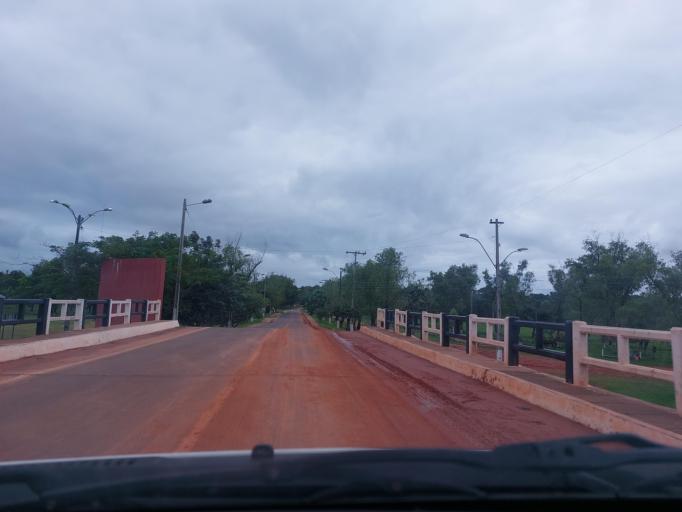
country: PY
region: San Pedro
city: Guayaybi
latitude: -24.6539
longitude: -56.4370
